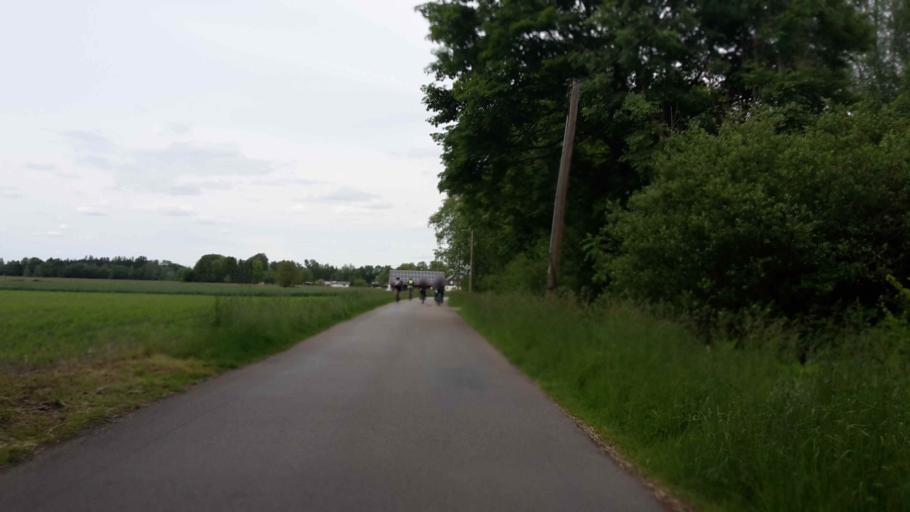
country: DE
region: Bavaria
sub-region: Upper Bavaria
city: Karlsfeld
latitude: 48.2165
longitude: 11.4343
